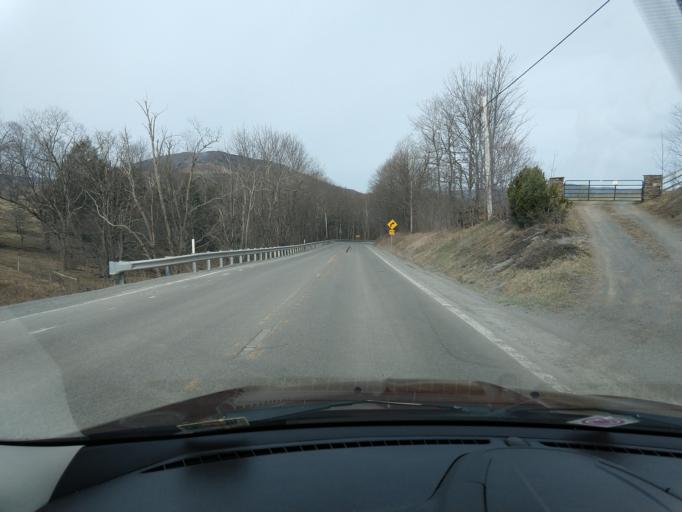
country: US
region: West Virginia
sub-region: Pendleton County
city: Franklin
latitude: 38.8948
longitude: -79.4719
